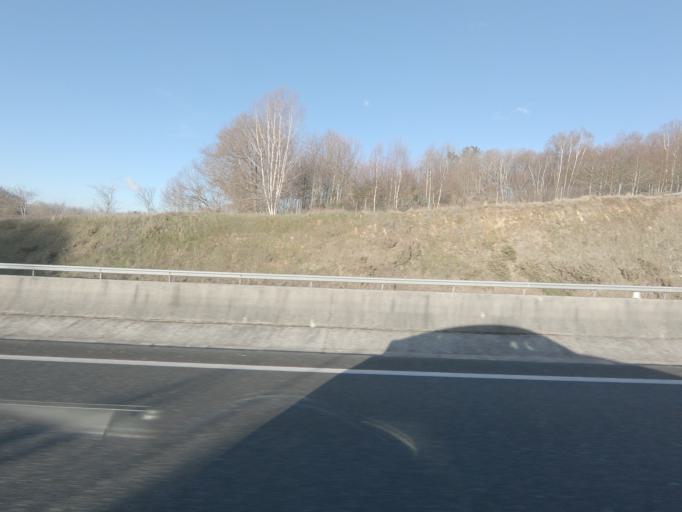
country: ES
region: Galicia
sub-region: Provincia de Pontevedra
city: Lalin
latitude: 42.6261
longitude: -8.1157
